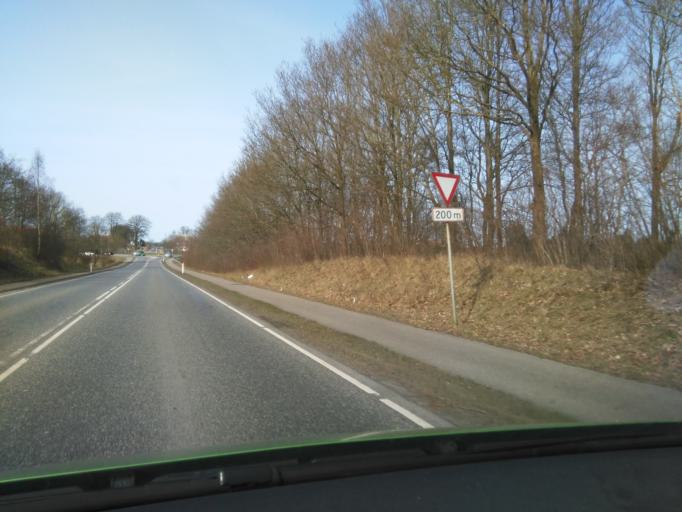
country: DK
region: Central Jutland
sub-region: Silkeborg Kommune
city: Silkeborg
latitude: 56.1940
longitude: 9.5282
